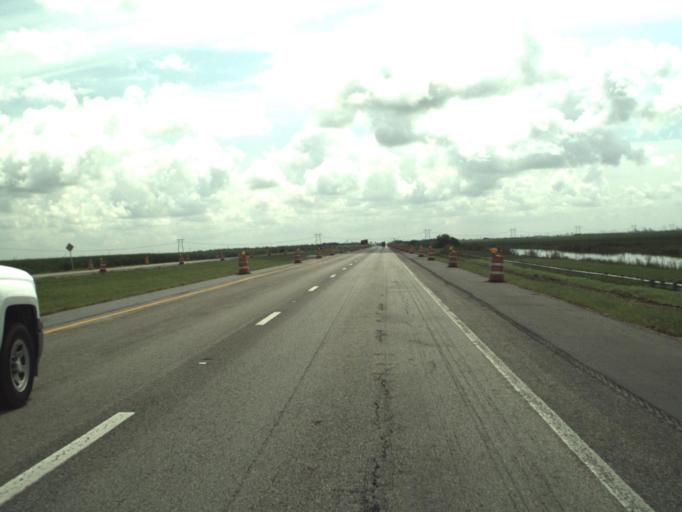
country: US
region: Florida
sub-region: Palm Beach County
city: Loxahatchee Groves
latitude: 26.7254
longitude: -80.4716
